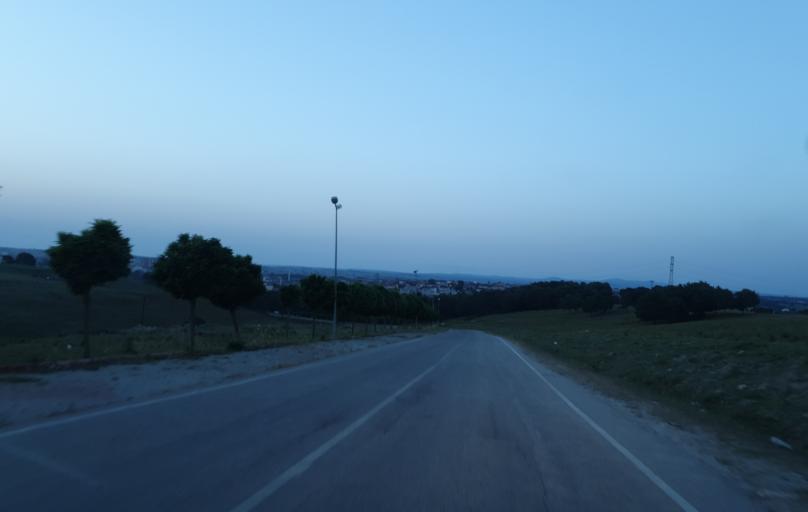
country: TR
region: Tekirdag
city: Saray
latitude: 41.3611
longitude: 27.9278
